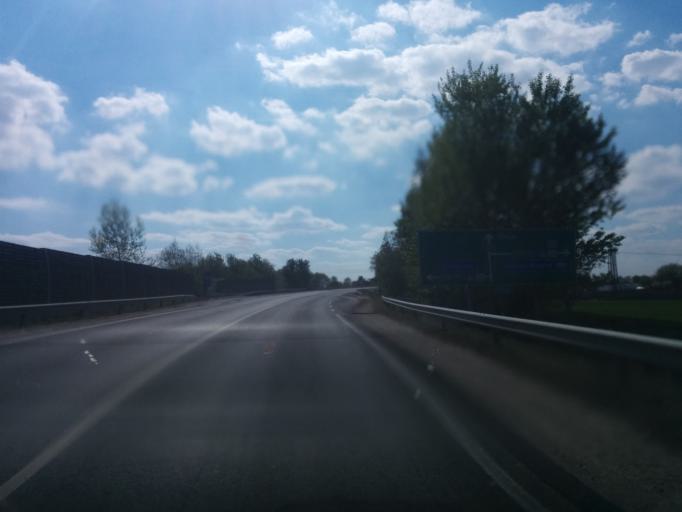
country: HU
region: Csongrad
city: Domaszek
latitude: 46.2482
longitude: 20.0431
